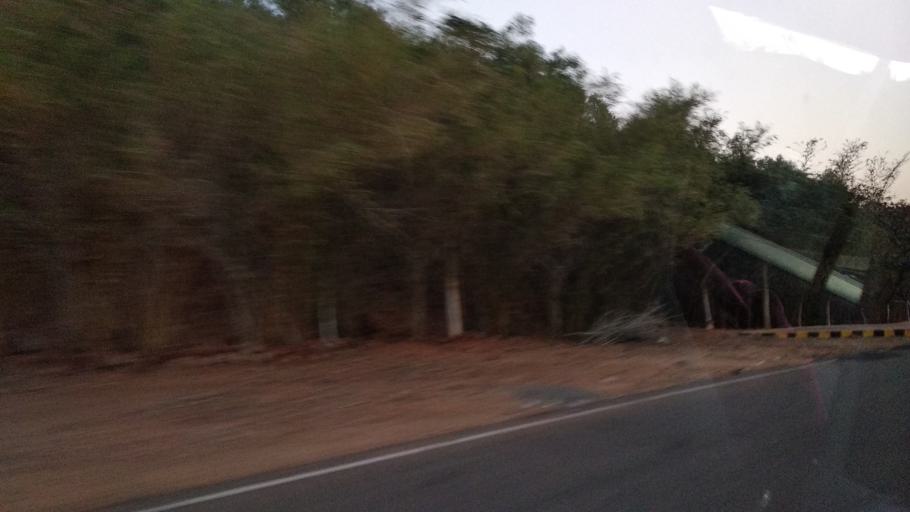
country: IN
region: Andhra Pradesh
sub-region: Vishakhapatnam
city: Bhimunipatnam
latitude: 17.7805
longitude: 83.3803
